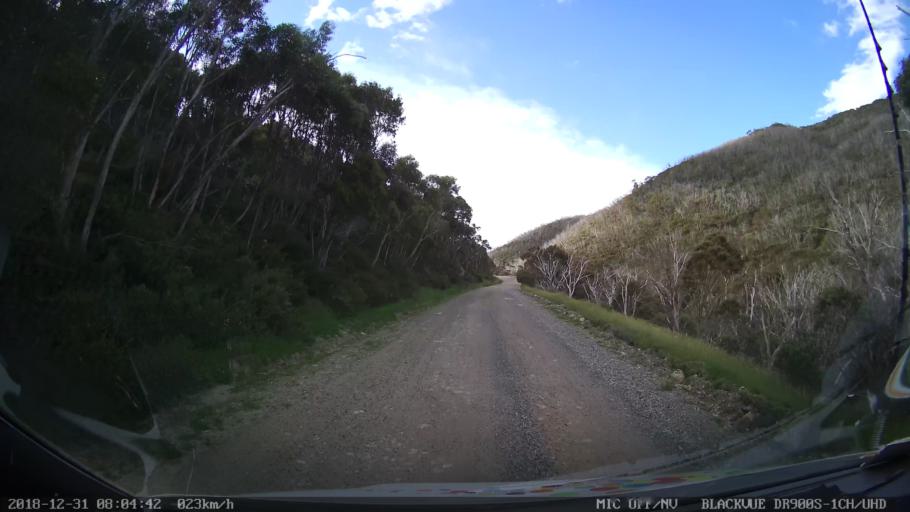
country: AU
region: New South Wales
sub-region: Snowy River
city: Jindabyne
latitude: -36.3685
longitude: 148.4064
